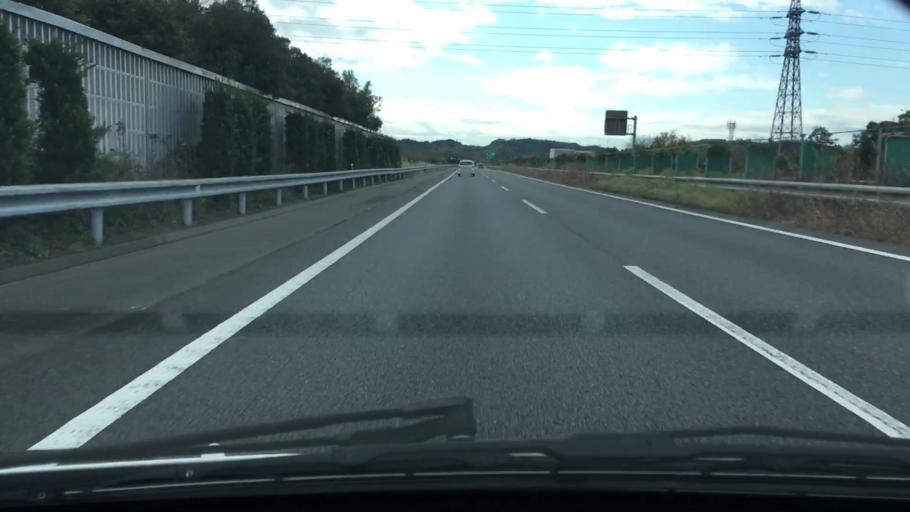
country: JP
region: Chiba
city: Kisarazu
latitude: 35.3990
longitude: 140.0062
